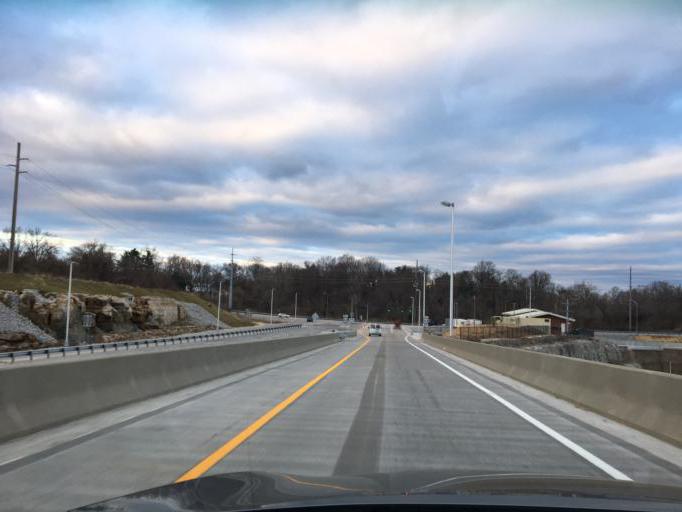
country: US
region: Kentucky
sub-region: Jefferson County
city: Prospect
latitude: 38.3231
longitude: -85.6194
